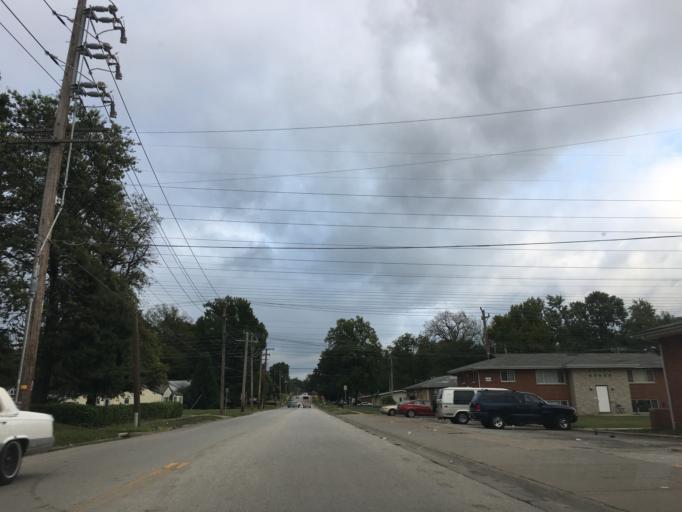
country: US
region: Missouri
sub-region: Saint Louis County
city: Berkeley
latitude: 38.7624
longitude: -90.3355
